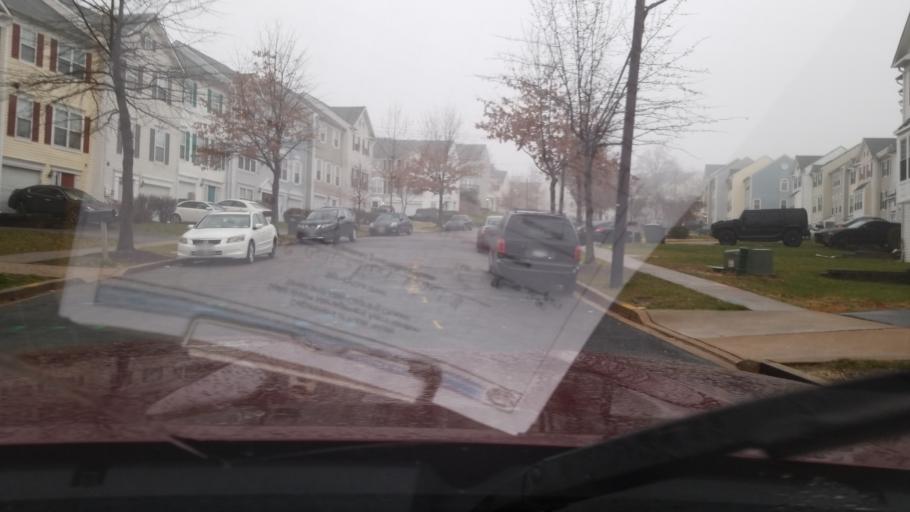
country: US
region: Maryland
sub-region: Prince George's County
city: Hillcrest Heights
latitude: 38.8449
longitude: -76.9742
